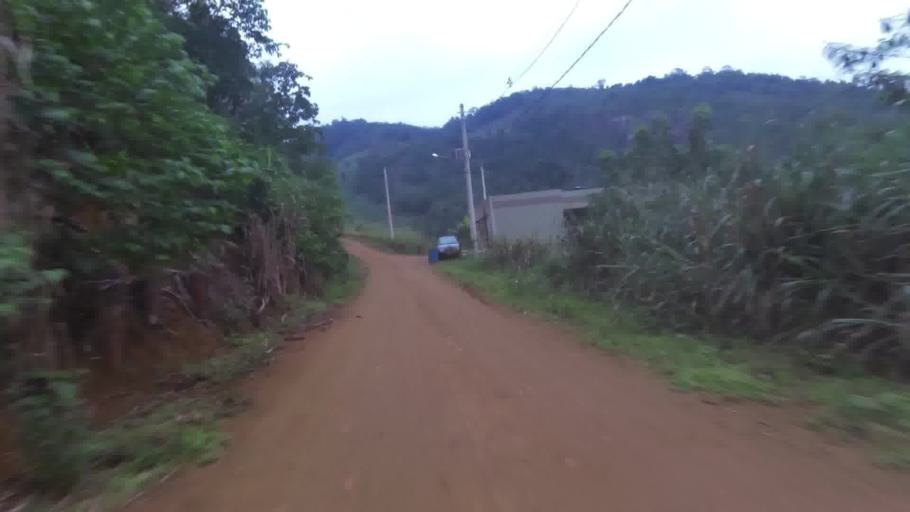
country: BR
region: Espirito Santo
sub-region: Iconha
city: Iconha
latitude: -20.7871
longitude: -40.8135
